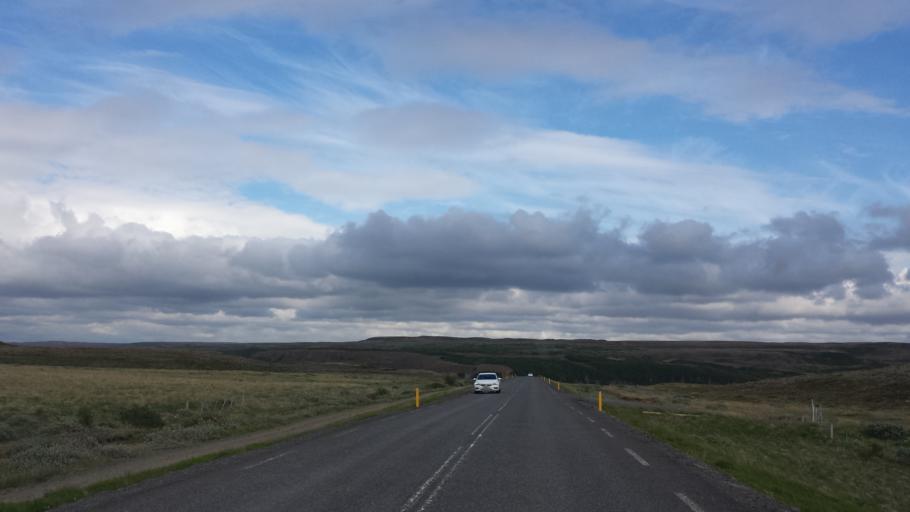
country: IS
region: South
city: Vestmannaeyjar
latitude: 64.3055
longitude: -20.1797
